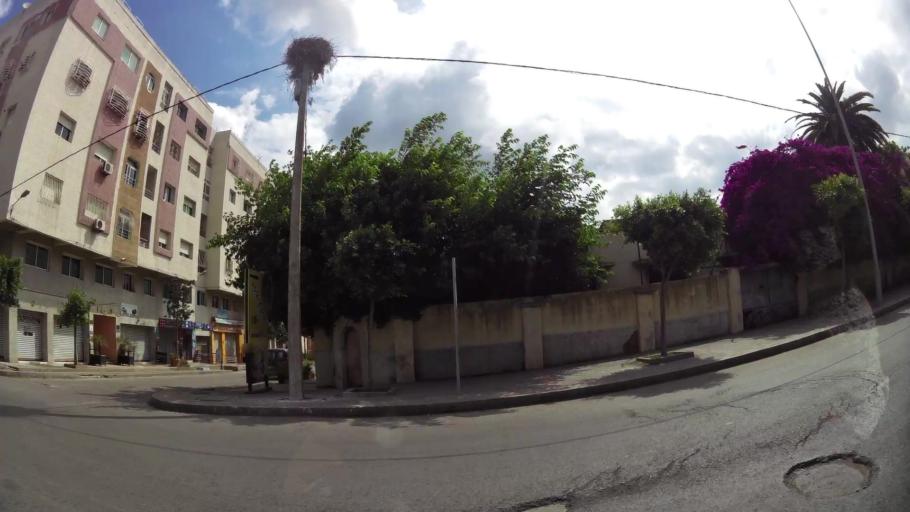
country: MA
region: Gharb-Chrarda-Beni Hssen
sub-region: Kenitra Province
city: Kenitra
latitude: 34.2657
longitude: -6.5710
